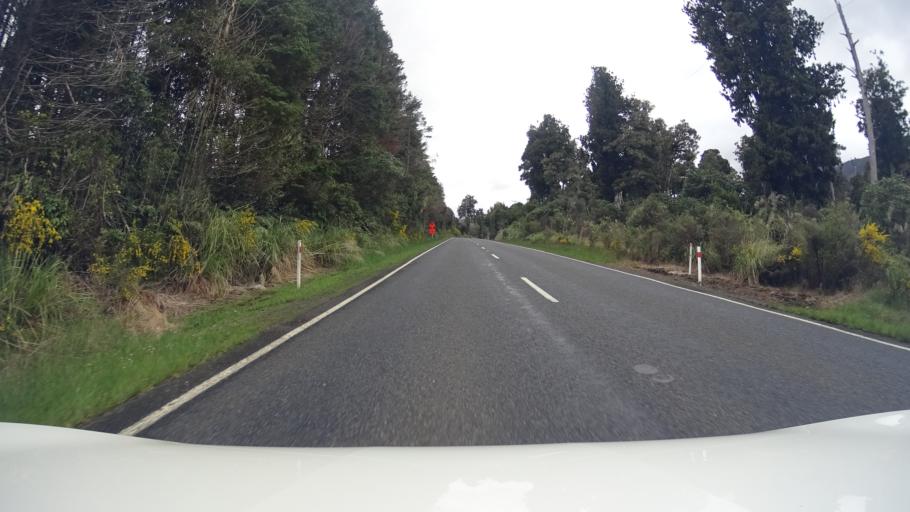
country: NZ
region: Manawatu-Wanganui
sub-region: Ruapehu District
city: Waiouru
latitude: -39.2381
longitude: 175.3916
